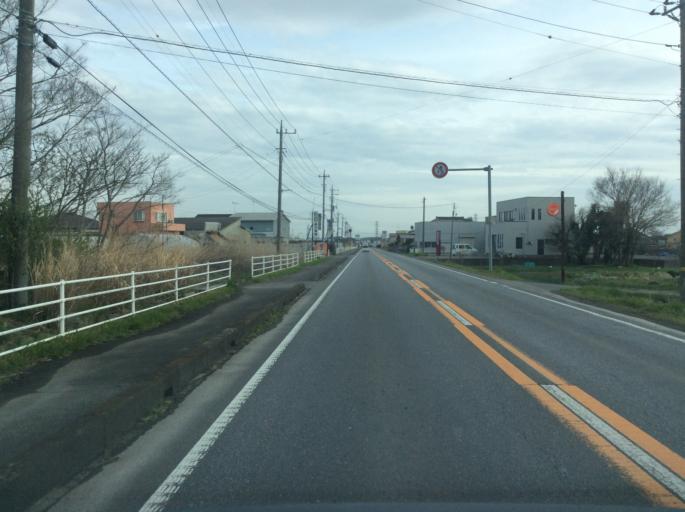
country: JP
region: Ibaraki
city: Tsukuba
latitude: 36.1510
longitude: 140.1170
